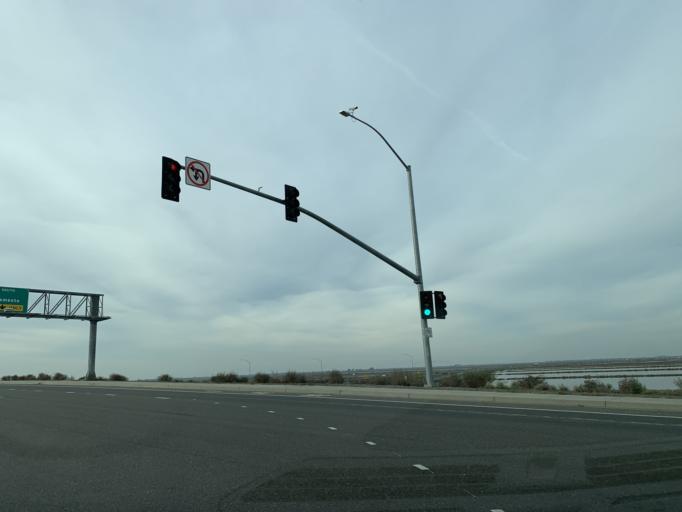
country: US
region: California
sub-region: Sacramento County
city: Elverta
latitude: 38.7504
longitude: -121.5387
